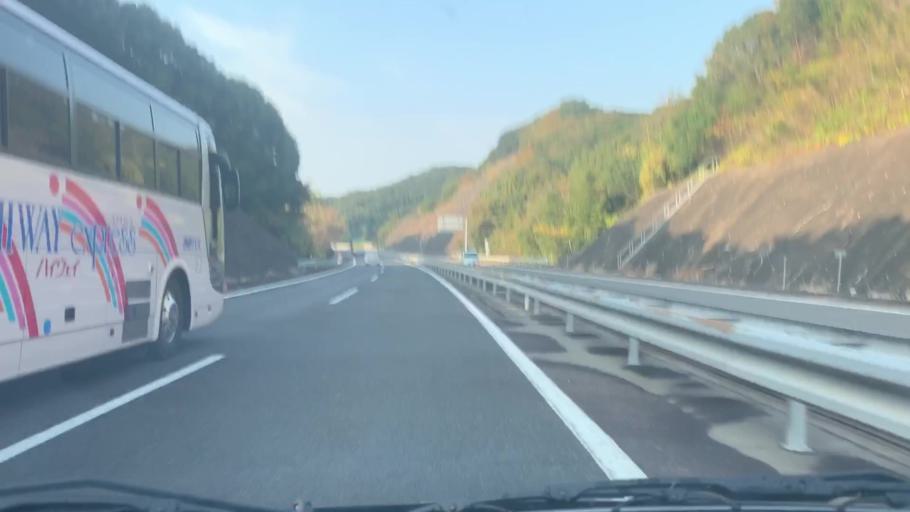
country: JP
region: Saga Prefecture
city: Imaricho-ko
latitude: 33.1695
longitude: 129.8415
